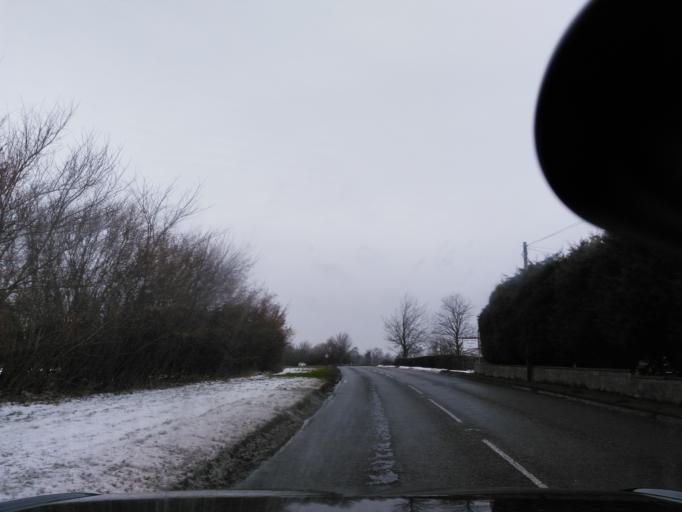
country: GB
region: England
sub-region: Wiltshire
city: Chippenham
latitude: 51.4391
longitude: -2.1316
